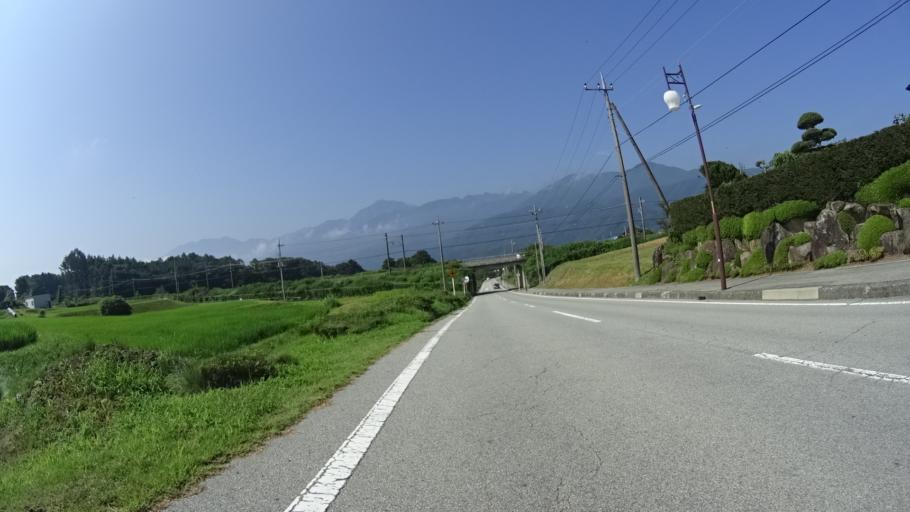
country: JP
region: Nagano
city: Chino
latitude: 35.8715
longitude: 138.3023
